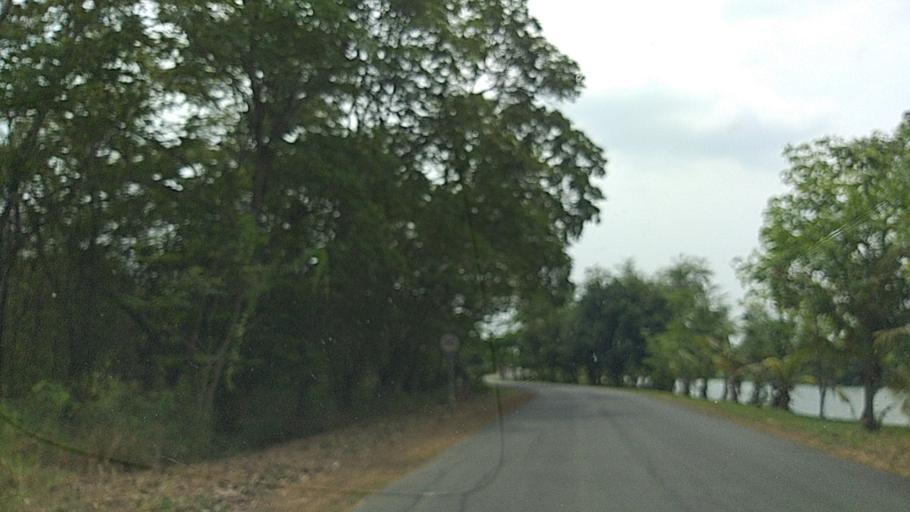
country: TH
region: Bangkok
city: Thawi Watthana
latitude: 13.7771
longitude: 100.3109
